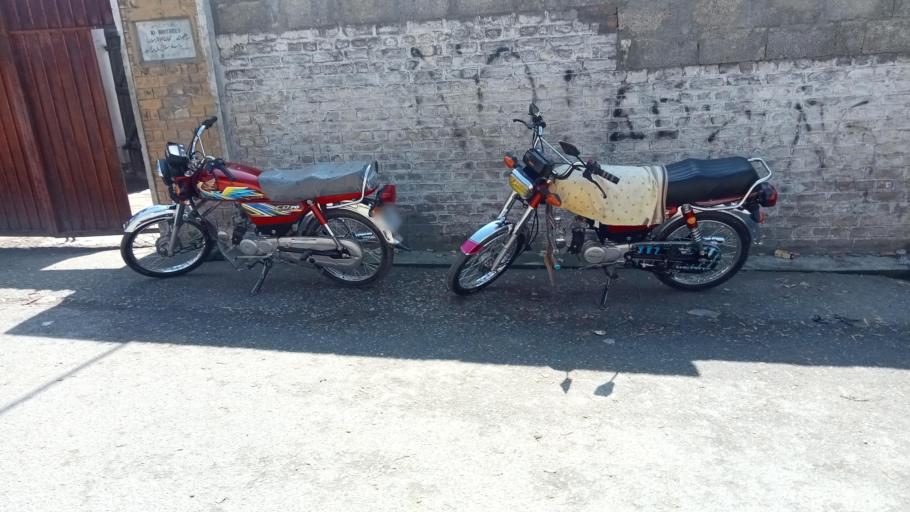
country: PK
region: Khyber Pakhtunkhwa
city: Saidu Sharif
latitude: 34.7597
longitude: 72.3591
